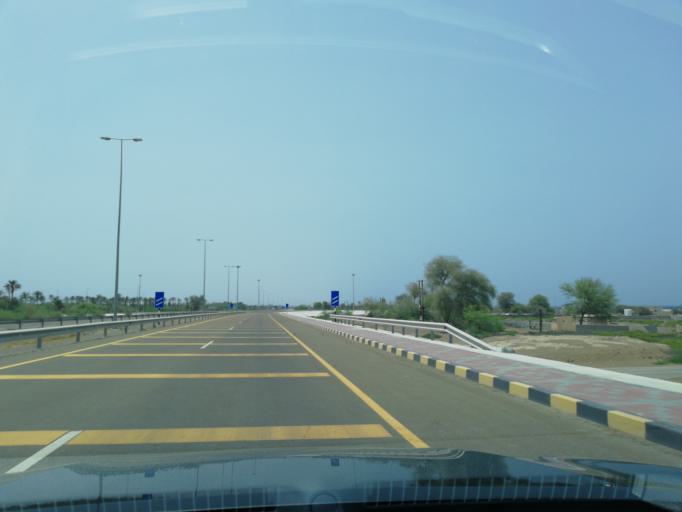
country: OM
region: Al Batinah
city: Al Liwa'
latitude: 24.6391
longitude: 56.5219
